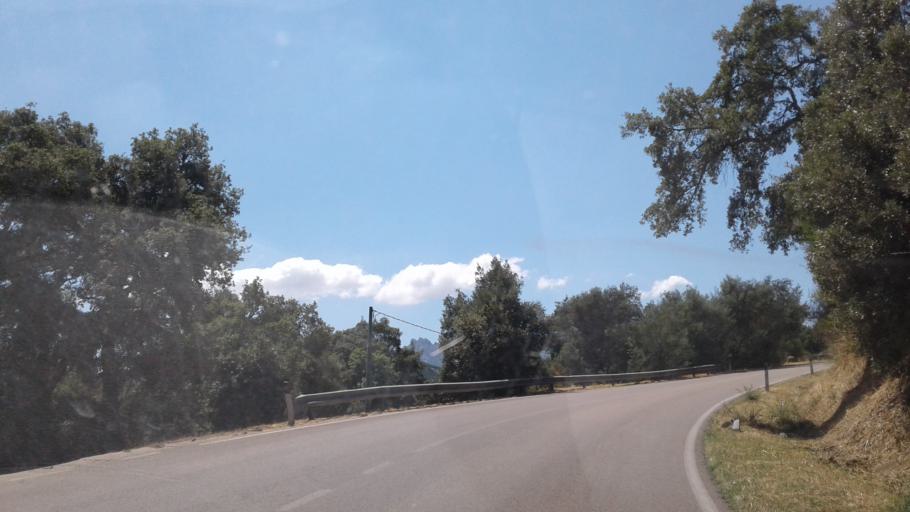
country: IT
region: Sardinia
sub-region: Provincia di Olbia-Tempio
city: Luras
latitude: 40.9309
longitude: 9.1817
